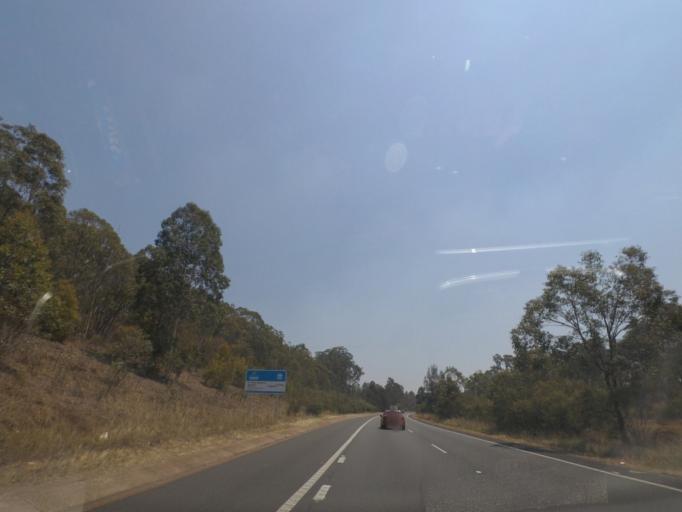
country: AU
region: New South Wales
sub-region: Newcastle
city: Beresfield
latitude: -32.8308
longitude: 151.6338
